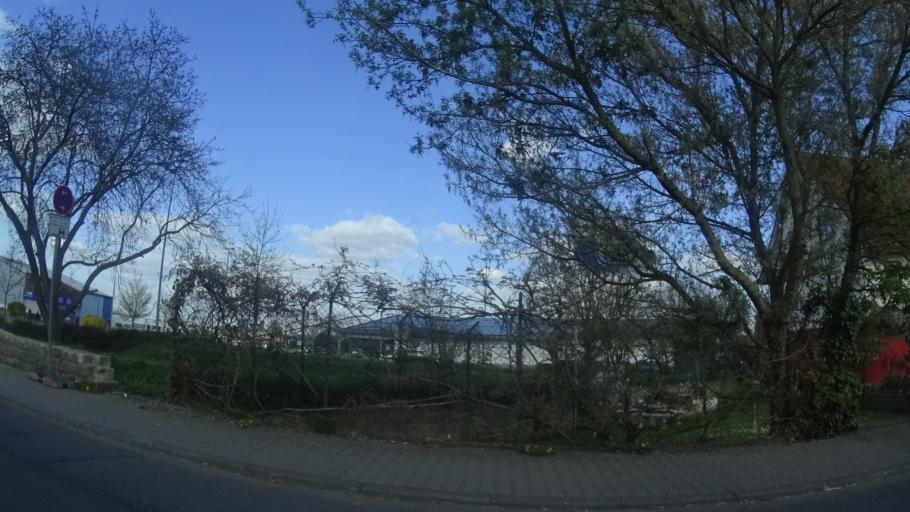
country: DE
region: Rheinland-Pfalz
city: Guntersblum
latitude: 49.8005
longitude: 8.3441
